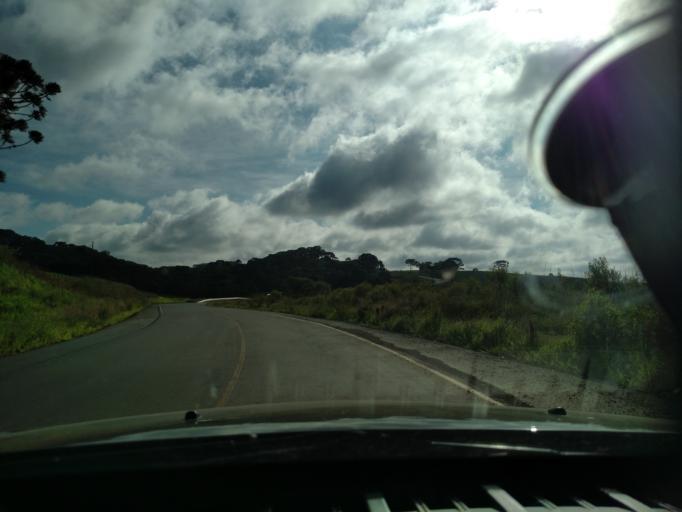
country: BR
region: Rio Grande do Sul
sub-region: Vacaria
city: Estrela
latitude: -27.9212
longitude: -50.6705
